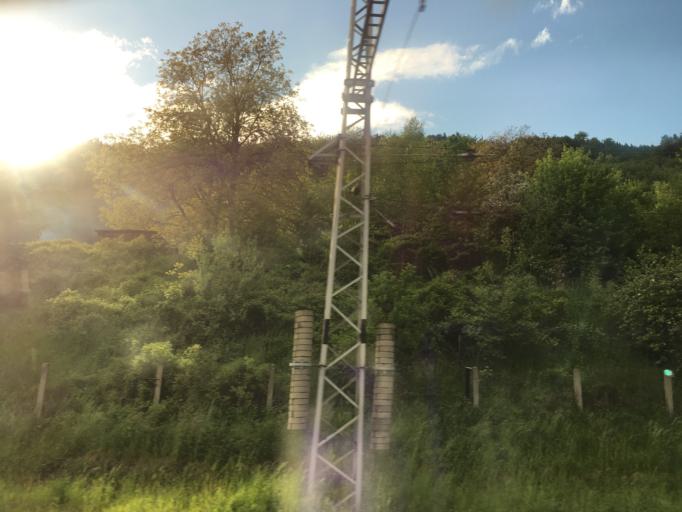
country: CZ
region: Ustecky
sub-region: Okres Decin
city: Decin
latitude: 50.7920
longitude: 14.2293
